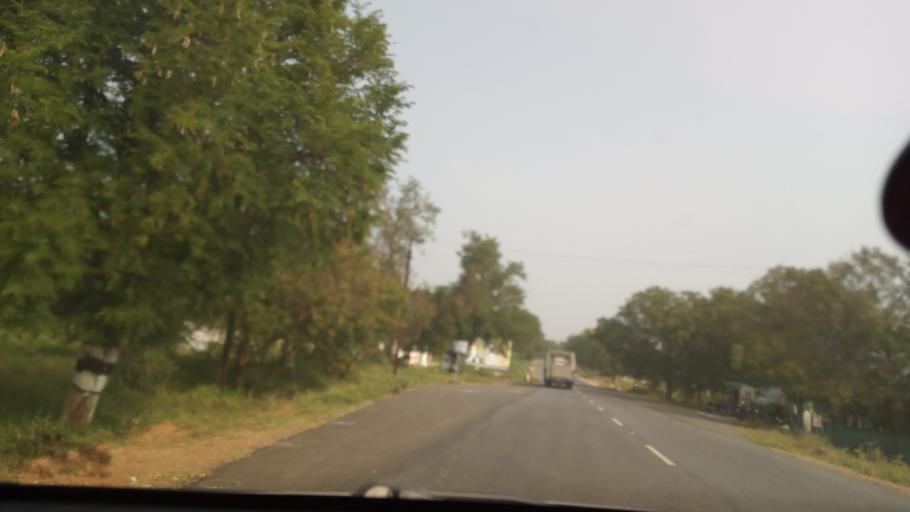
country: IN
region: Tamil Nadu
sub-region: Erode
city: Punjai Puliyampatti
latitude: 11.4125
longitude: 77.1931
